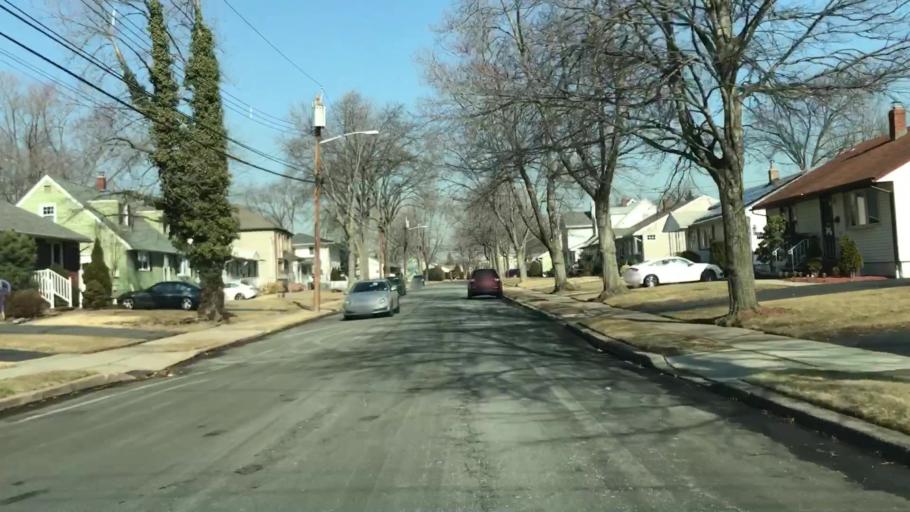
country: US
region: New Jersey
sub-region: Bergen County
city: Hasbrouck Heights
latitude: 40.8558
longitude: -74.0726
